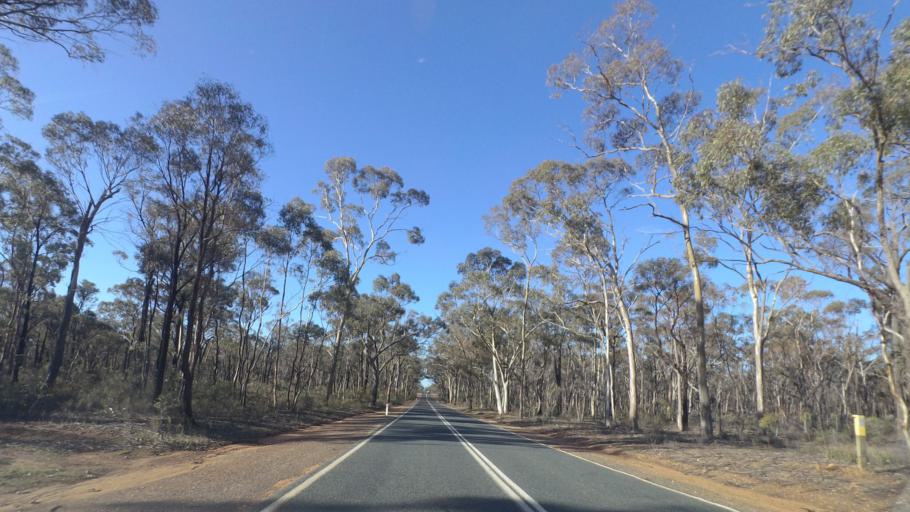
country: AU
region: Victoria
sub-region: Greater Bendigo
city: Epsom
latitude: -36.6674
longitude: 144.4306
